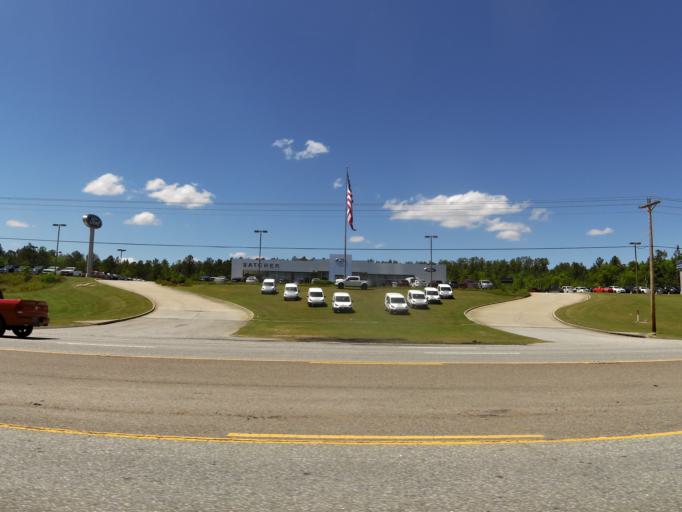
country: US
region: South Carolina
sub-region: Aiken County
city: Gloverville
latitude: 33.5405
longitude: -81.8297
